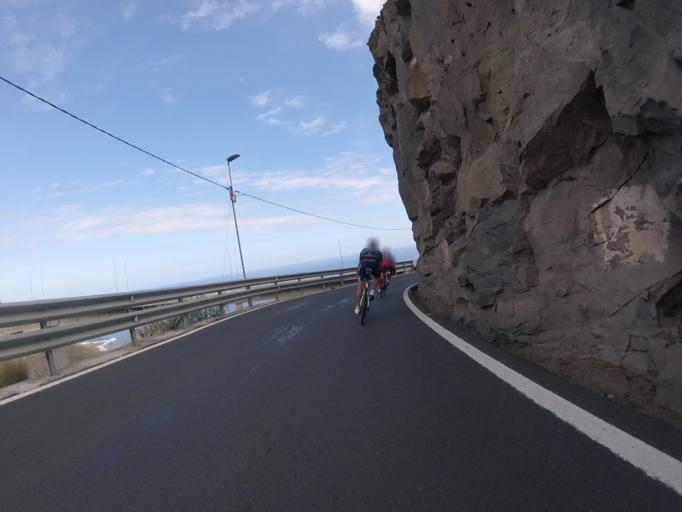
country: ES
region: Canary Islands
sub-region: Provincia de Las Palmas
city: Guia
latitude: 28.1387
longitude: -15.5967
